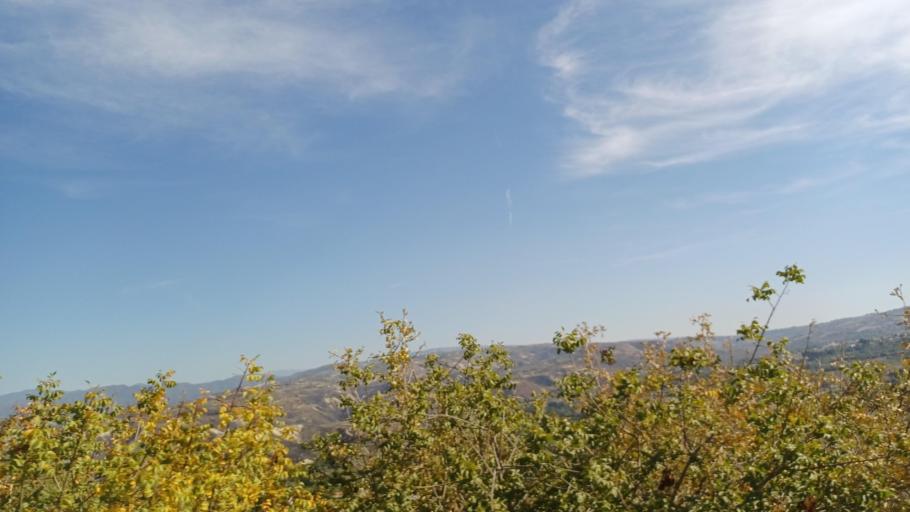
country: CY
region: Pafos
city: Pegeia
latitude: 34.9396
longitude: 32.4548
